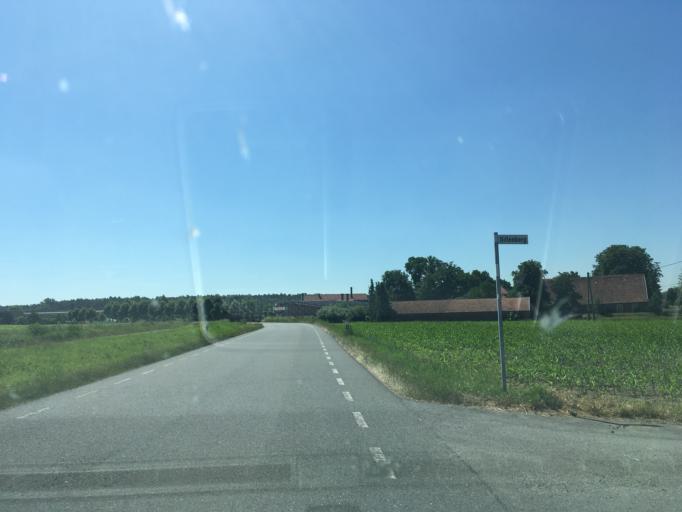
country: DE
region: North Rhine-Westphalia
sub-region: Regierungsbezirk Munster
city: Borken
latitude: 51.8232
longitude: 6.8013
